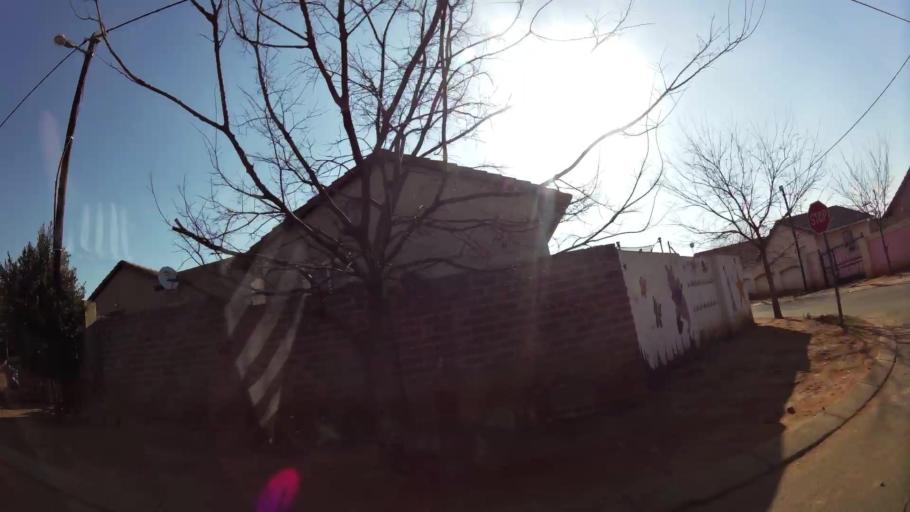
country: ZA
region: Gauteng
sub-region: West Rand District Municipality
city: Muldersdriseloop
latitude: -26.0300
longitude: 27.9164
